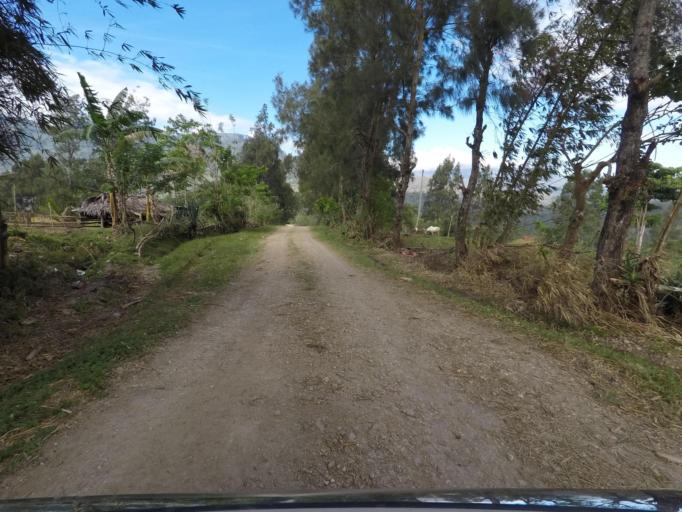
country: TL
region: Baucau
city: Venilale
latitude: -8.6511
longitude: 126.3922
